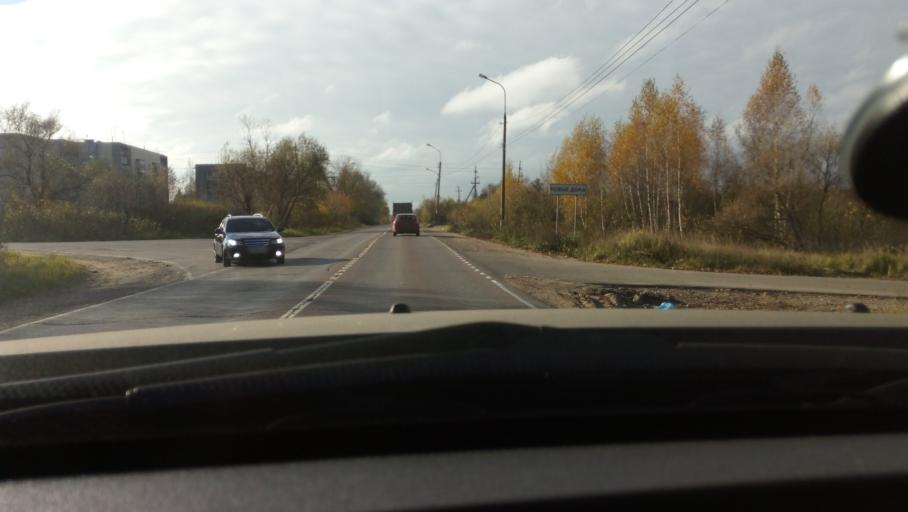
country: RU
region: Moskovskaya
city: Fryazevo
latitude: 55.7174
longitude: 38.4664
